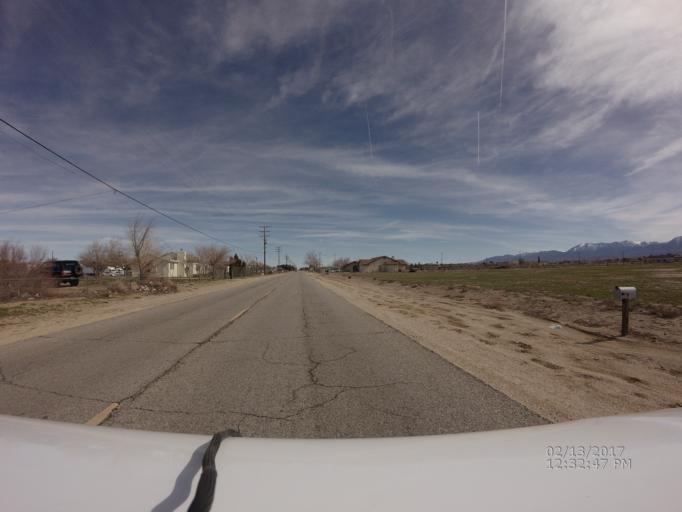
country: US
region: California
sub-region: Los Angeles County
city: Littlerock
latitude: 34.5724
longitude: -117.9585
